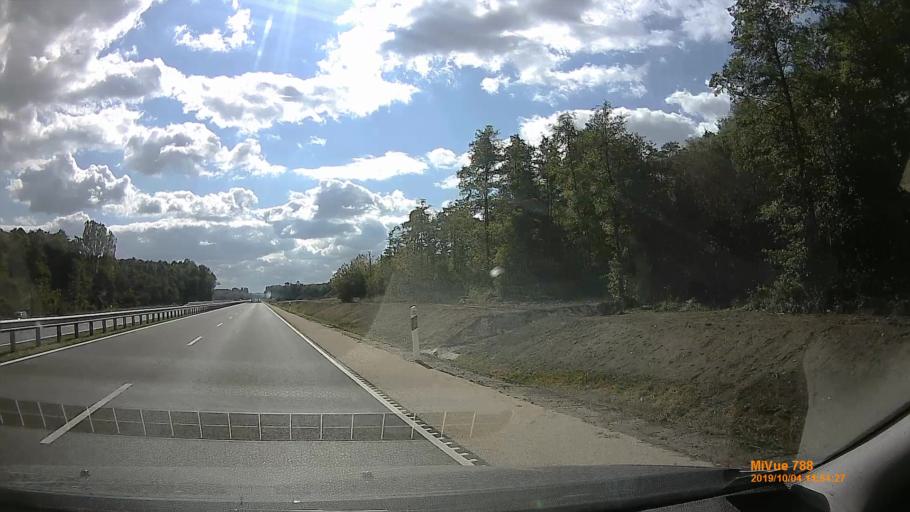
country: HU
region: Somogy
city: Karad
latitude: 46.6934
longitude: 17.7700
